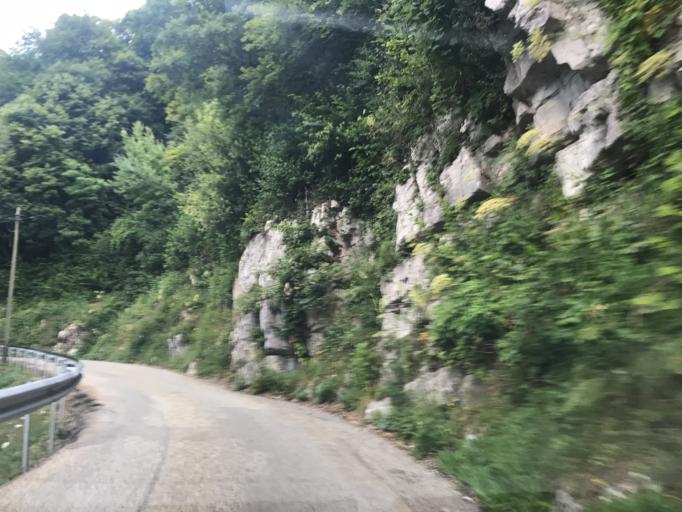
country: FR
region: Rhone-Alpes
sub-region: Departement de l'Isere
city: Saint-Vincent-de-Mercuze
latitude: 45.3922
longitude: 5.9492
